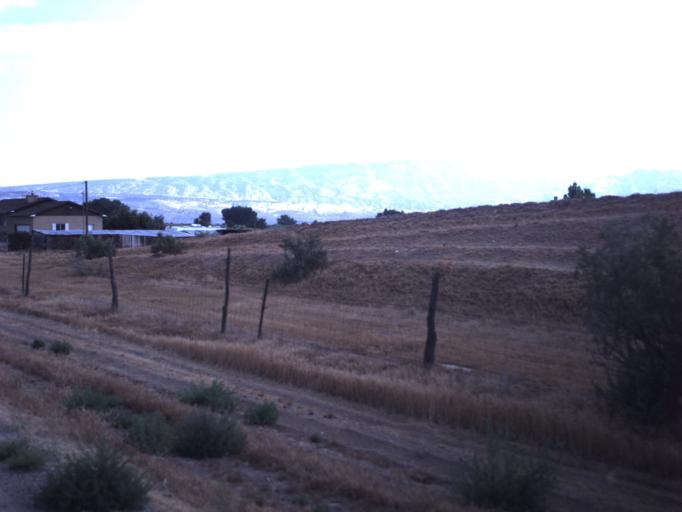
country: US
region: Utah
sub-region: Uintah County
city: Naples
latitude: 40.3909
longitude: -109.3460
